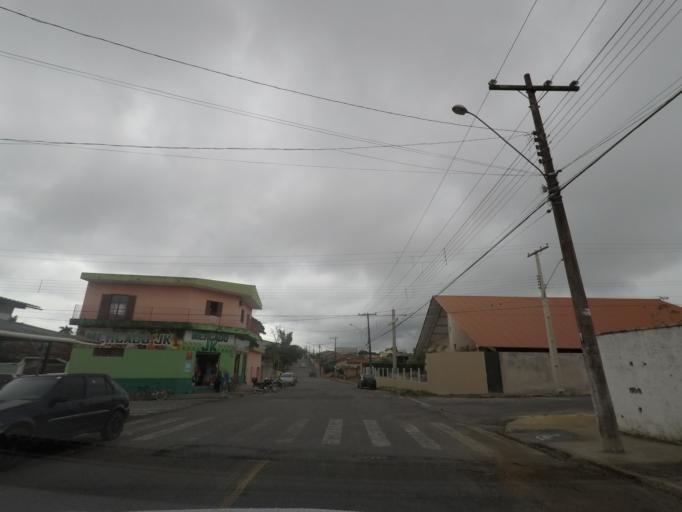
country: BR
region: Sao Paulo
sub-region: Registro
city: Registro
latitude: -24.5061
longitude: -47.8546
